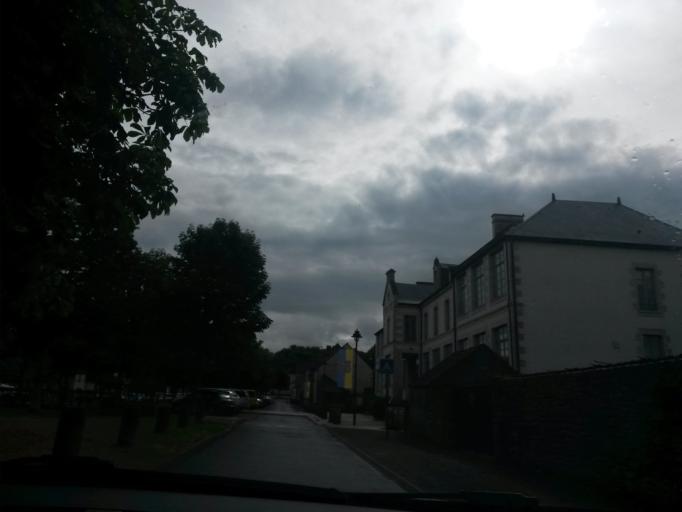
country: FR
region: Bourgogne
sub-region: Departement de la Nievre
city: Varzy
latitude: 47.3565
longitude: 3.3852
